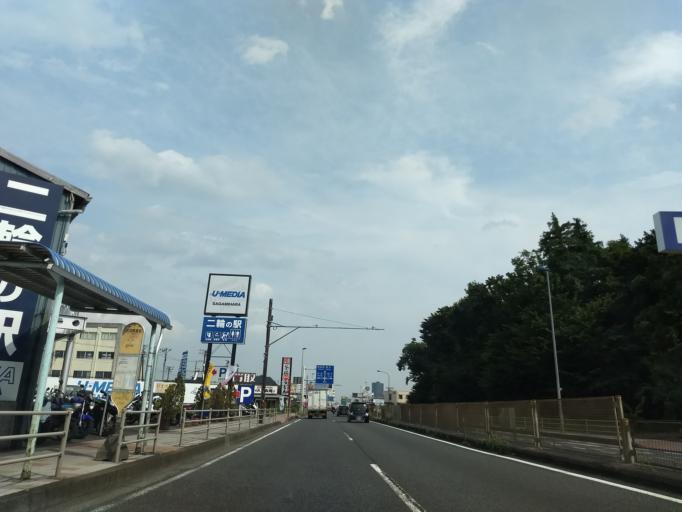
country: JP
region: Tokyo
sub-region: Machida-shi
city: Machida
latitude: 35.5454
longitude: 139.4269
